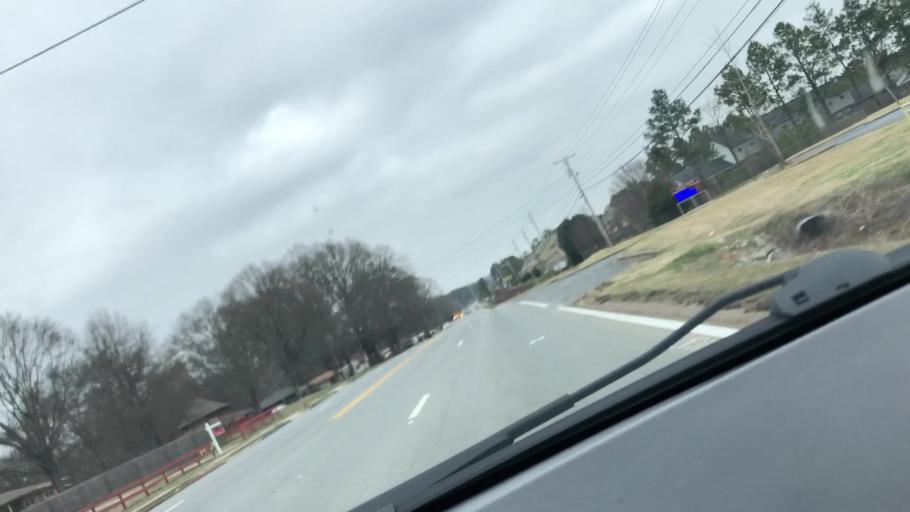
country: US
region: Georgia
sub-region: Bartow County
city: Cartersville
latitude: 34.2136
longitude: -84.8189
